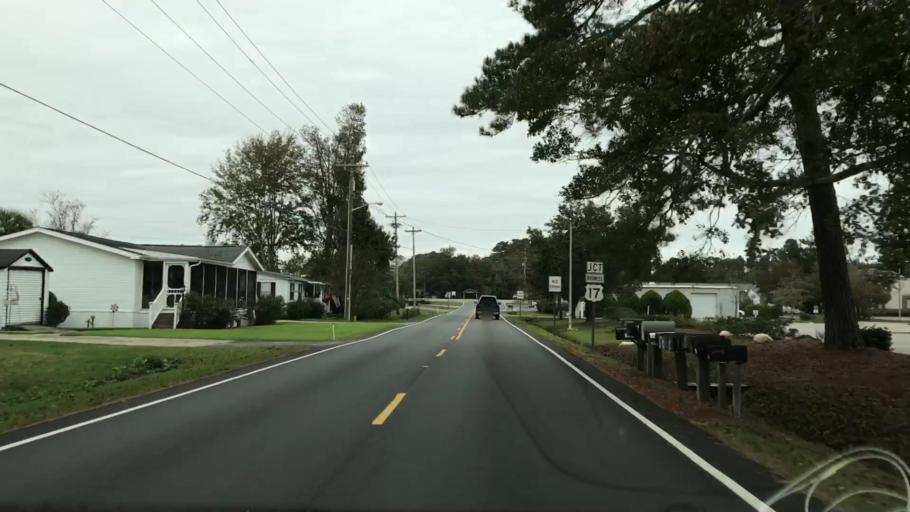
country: US
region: South Carolina
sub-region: Horry County
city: Garden City
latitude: 33.5889
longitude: -79.0046
